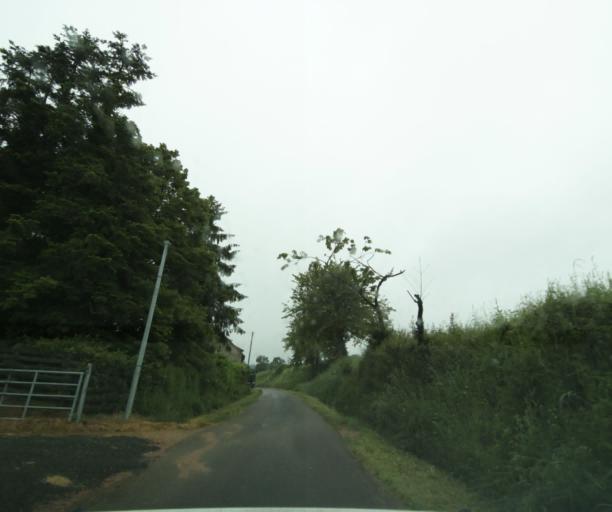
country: FR
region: Bourgogne
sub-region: Departement de Saone-et-Loire
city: Charolles
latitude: 46.3978
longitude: 4.3846
